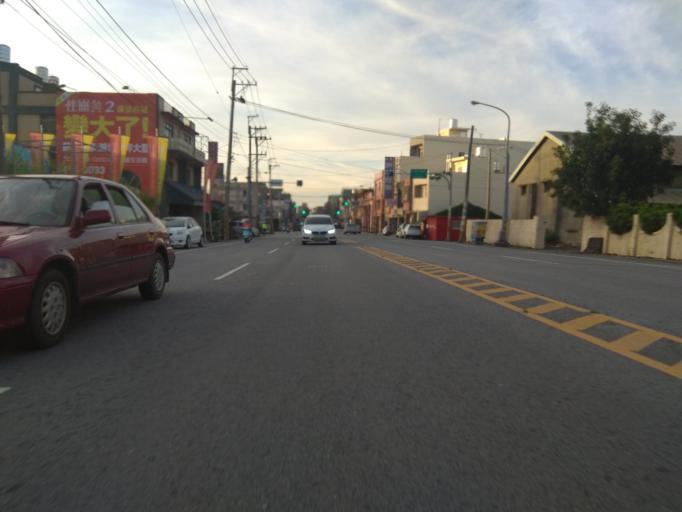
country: TW
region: Taiwan
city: Taoyuan City
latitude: 24.9871
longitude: 121.1832
